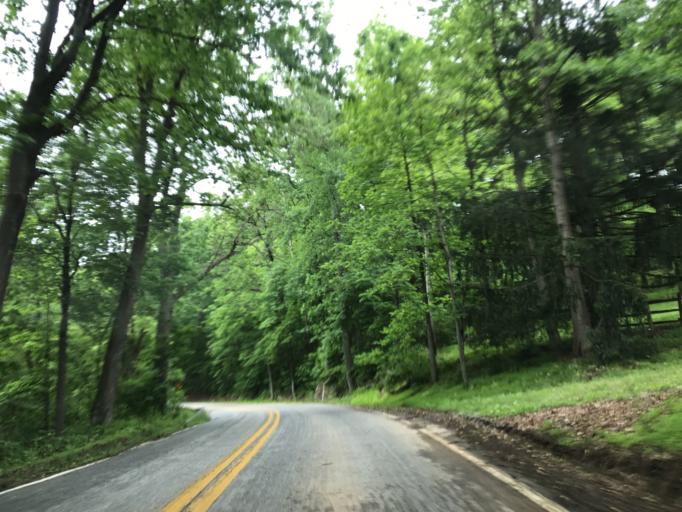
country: US
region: Pennsylvania
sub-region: York County
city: Susquehanna Trails
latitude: 39.7614
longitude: -76.4279
